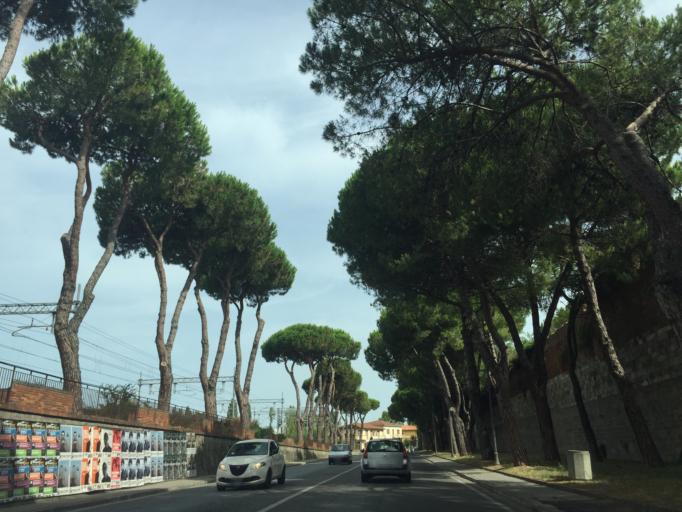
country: IT
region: Tuscany
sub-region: Province of Pisa
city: Pisa
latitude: 43.7141
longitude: 10.3885
